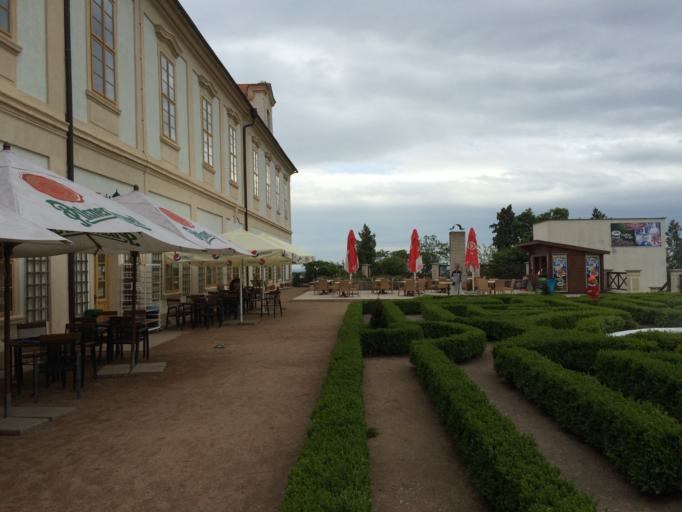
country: CZ
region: Central Bohemia
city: Loucen
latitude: 50.2870
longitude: 15.0239
